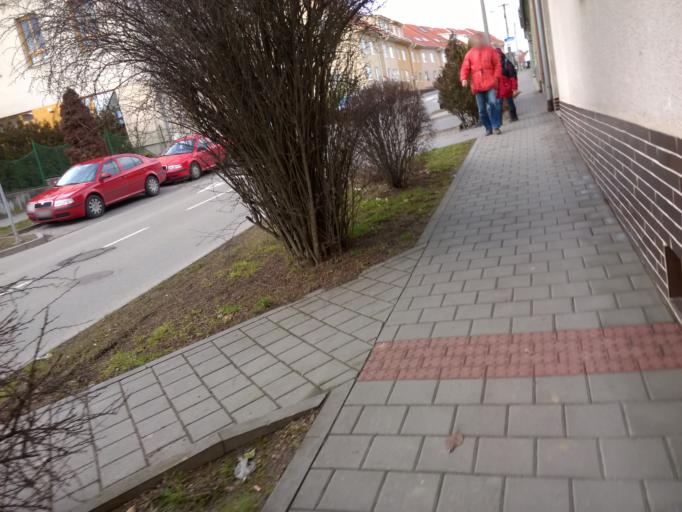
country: CZ
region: South Moravian
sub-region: Mesto Brno
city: Mokra Hora
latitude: 49.2553
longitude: 16.6227
